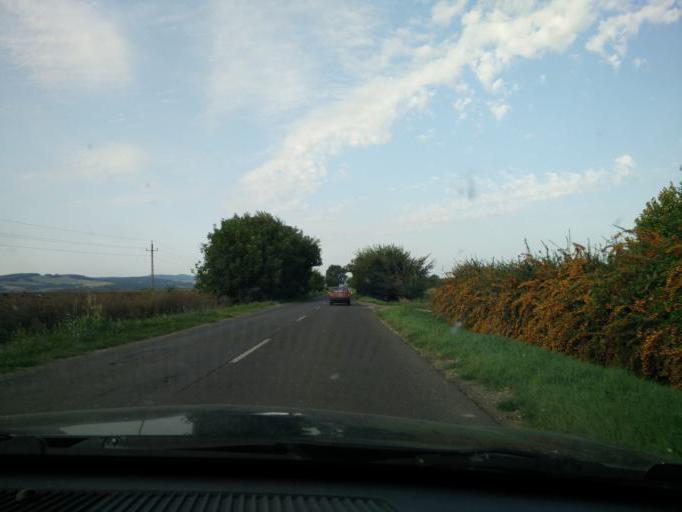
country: HU
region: Tolna
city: Bonyhad
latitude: 46.2974
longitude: 18.4944
